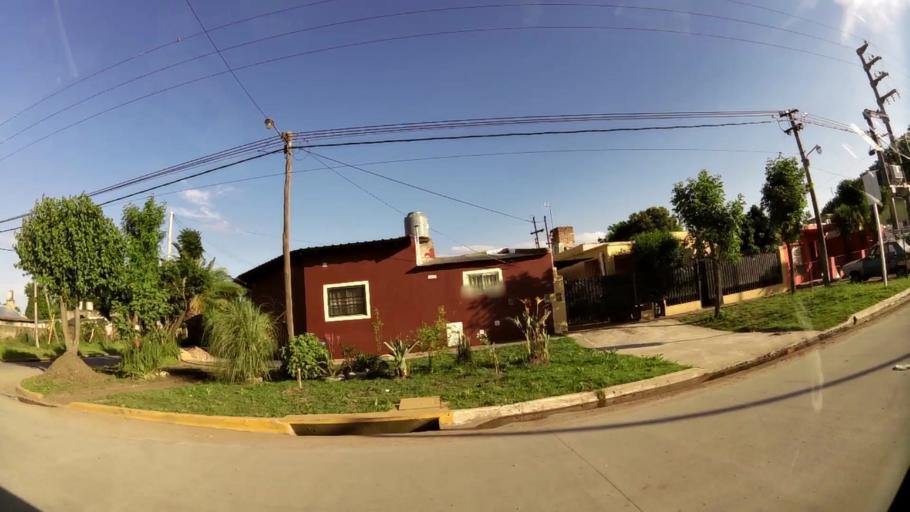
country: AR
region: Buenos Aires
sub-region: Partido de Merlo
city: Merlo
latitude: -34.6859
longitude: -58.7379
